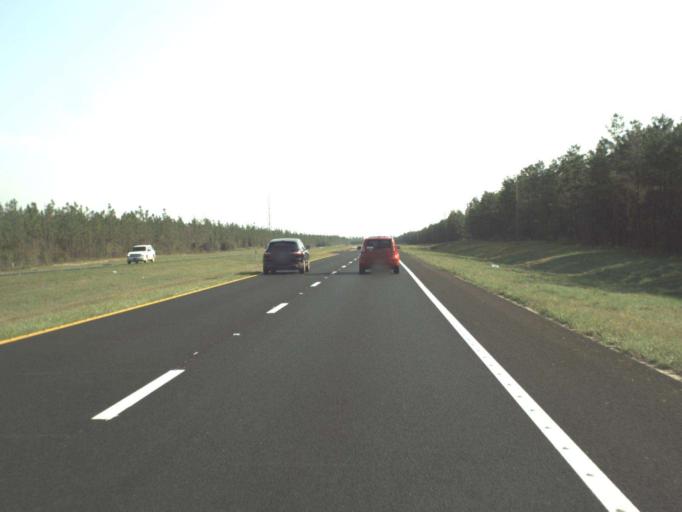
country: US
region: Florida
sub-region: Holmes County
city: Bonifay
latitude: 30.5546
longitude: -85.8194
